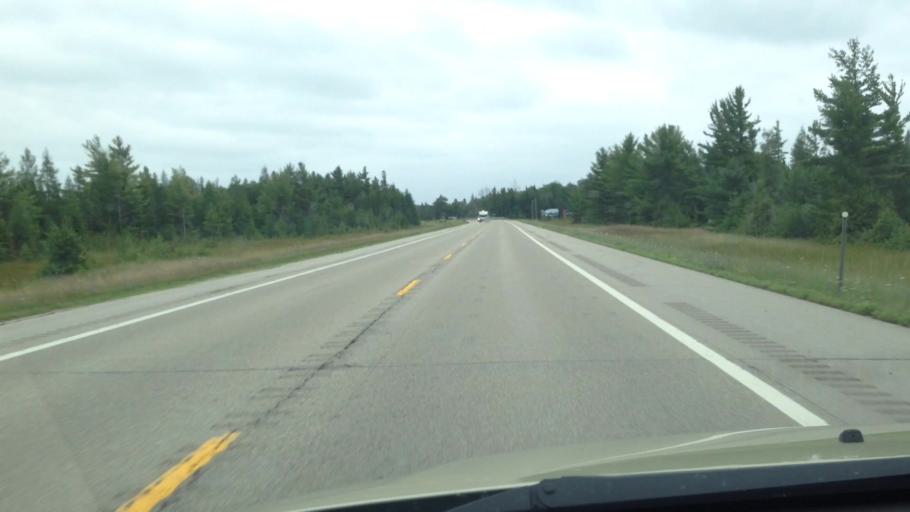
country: US
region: Michigan
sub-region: Mackinac County
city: Saint Ignace
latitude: 45.9198
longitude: -84.8761
